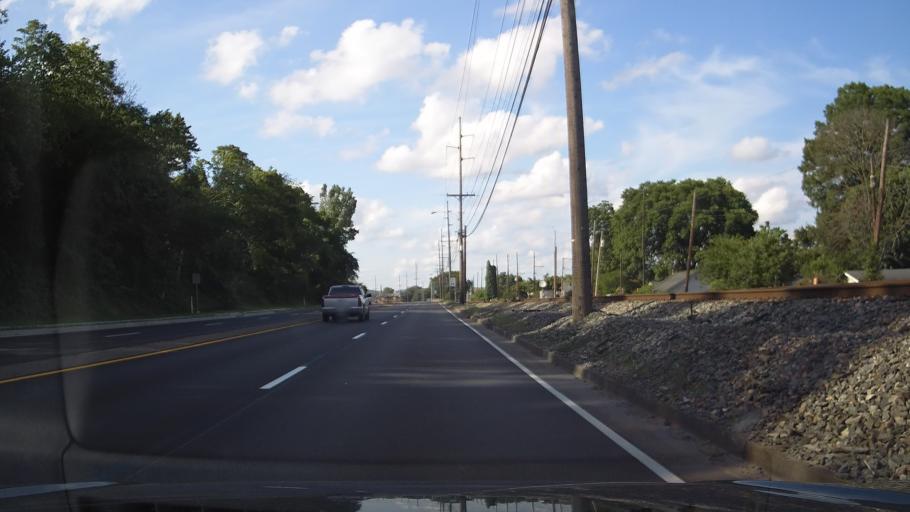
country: US
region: Kentucky
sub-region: Boyd County
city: Catlettsburg
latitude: 38.4092
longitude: -82.5996
